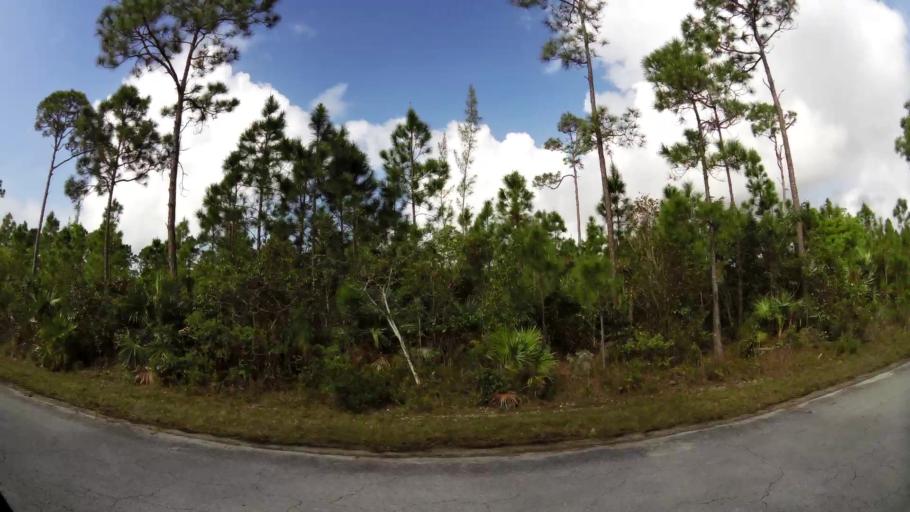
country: BS
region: Freeport
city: Lucaya
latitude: 26.5523
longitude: -78.5543
